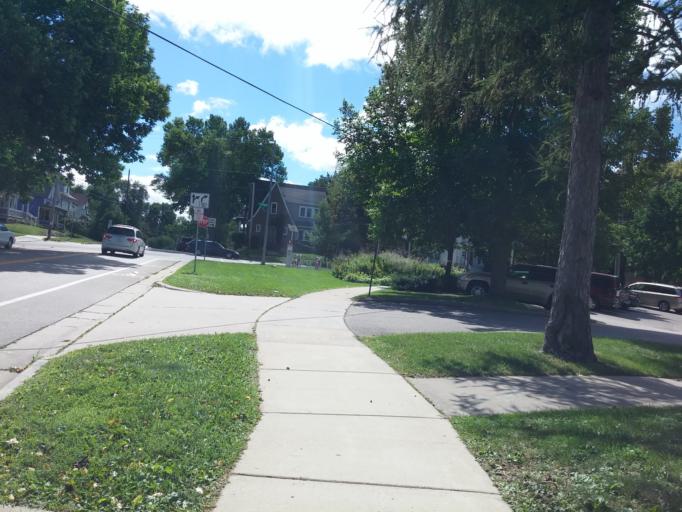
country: US
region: Wisconsin
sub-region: Dane County
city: Madison
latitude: 43.0866
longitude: -89.3759
